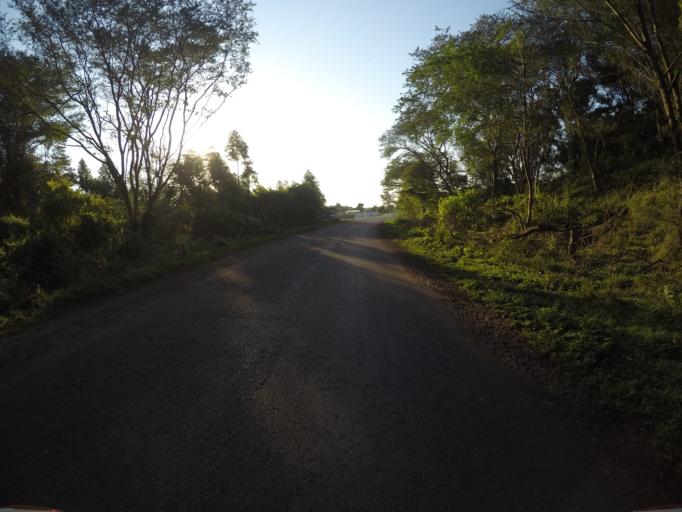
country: ZA
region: KwaZulu-Natal
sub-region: uThungulu District Municipality
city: KwaMbonambi
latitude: -28.6894
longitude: 32.2074
